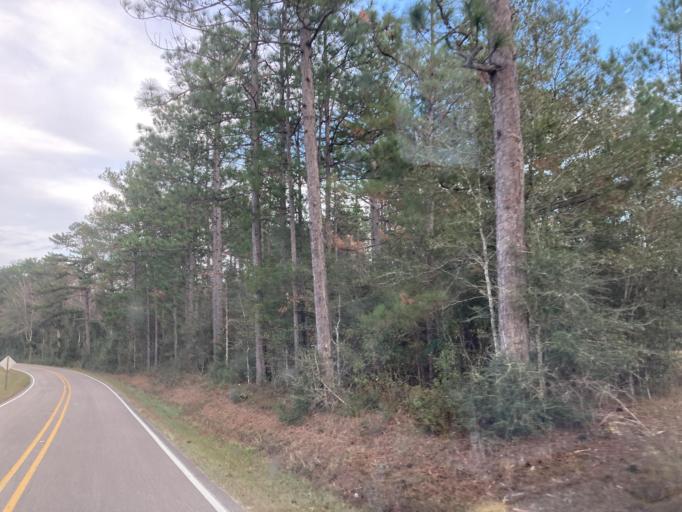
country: US
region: Mississippi
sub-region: Lamar County
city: Purvis
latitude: 31.1840
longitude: -89.3517
